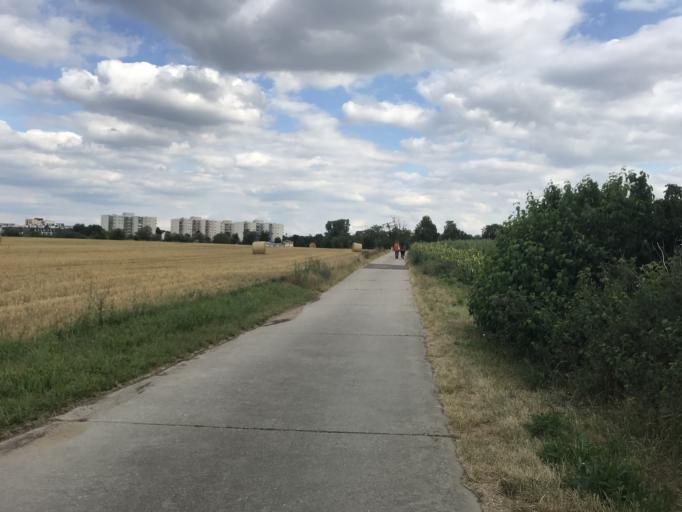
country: DE
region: Hesse
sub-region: Regierungsbezirk Darmstadt
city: Hochheim am Main
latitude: 50.0225
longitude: 8.3371
